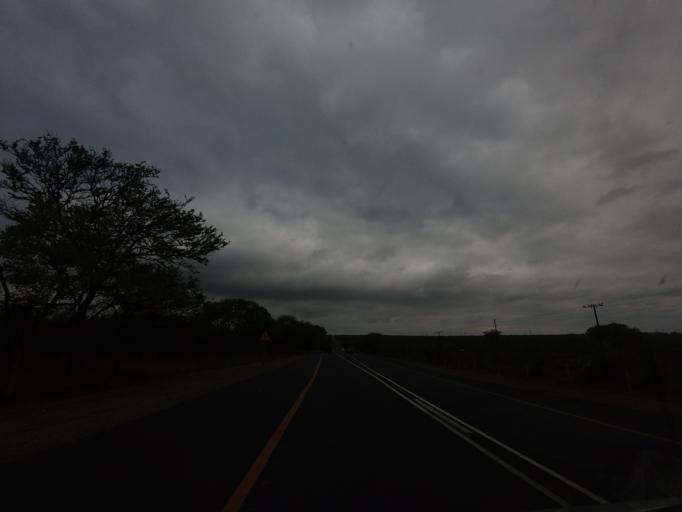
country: ZA
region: Mpumalanga
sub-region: Ehlanzeni District
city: Komatipoort
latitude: -25.4407
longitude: 31.7315
